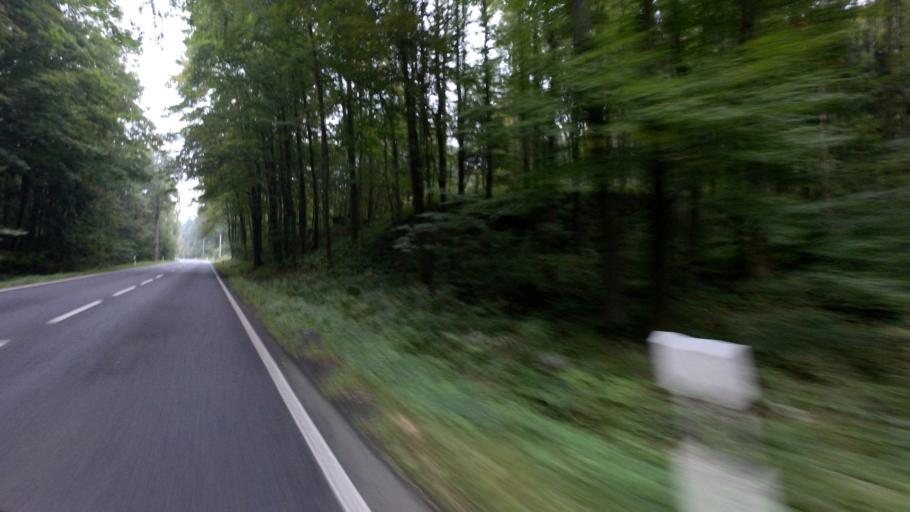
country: DE
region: Saxony
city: Sebnitz
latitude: 50.9913
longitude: 14.2430
